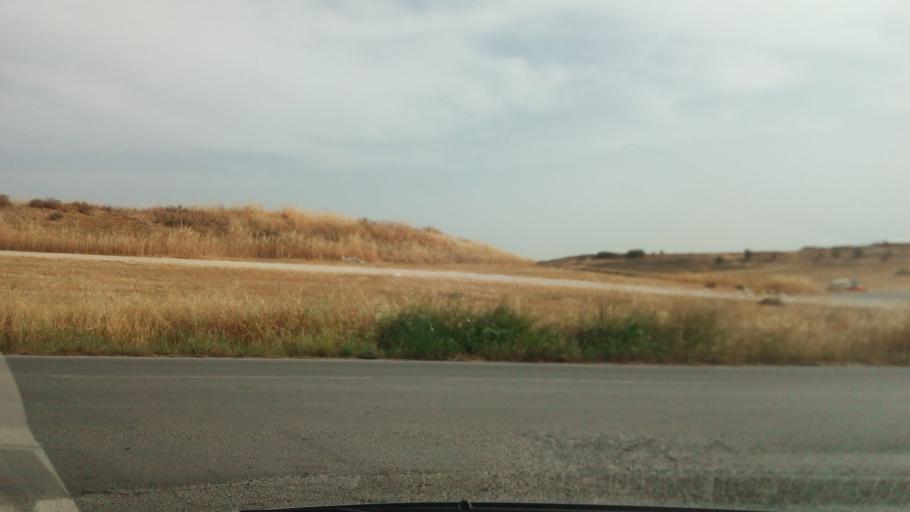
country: CY
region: Larnaka
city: Livadia
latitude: 34.9518
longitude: 33.6121
